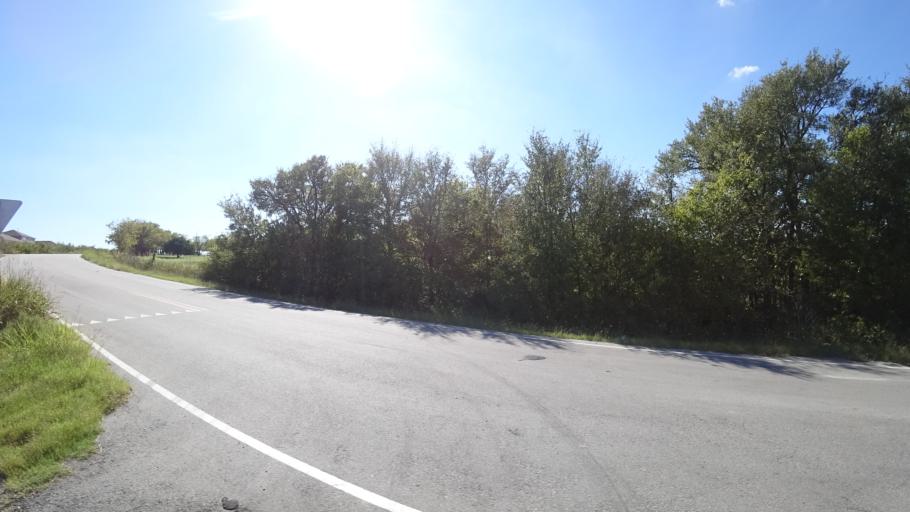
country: US
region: Texas
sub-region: Travis County
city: Manor
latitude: 30.3593
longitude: -97.6061
